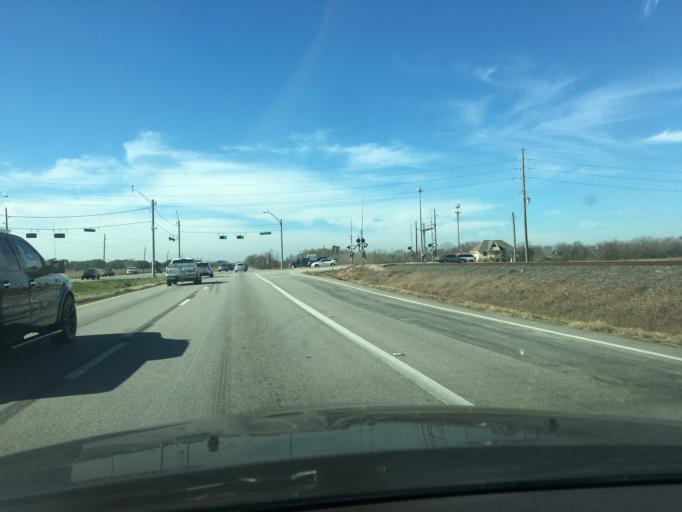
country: US
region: Texas
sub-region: Fort Bend County
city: New Territory
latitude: 29.5990
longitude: -95.7125
